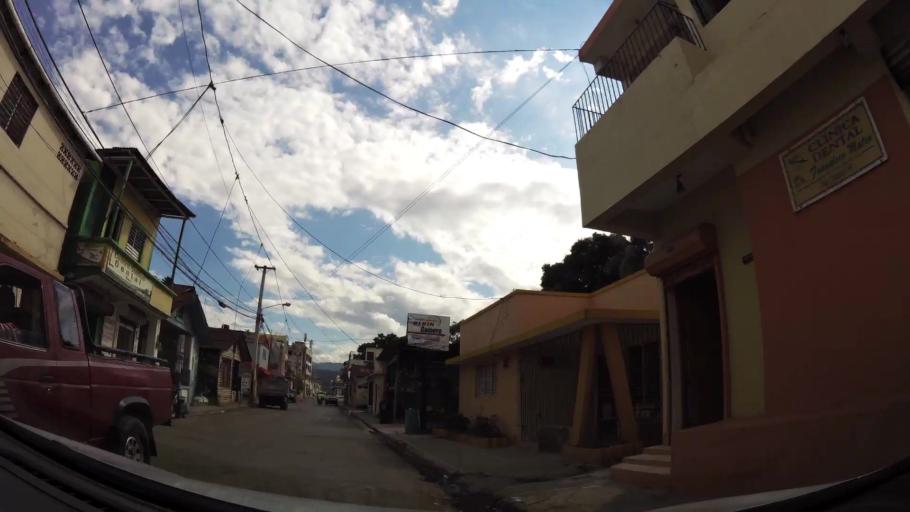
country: DO
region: La Vega
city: Concepcion de La Vega
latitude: 19.2277
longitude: -70.5333
